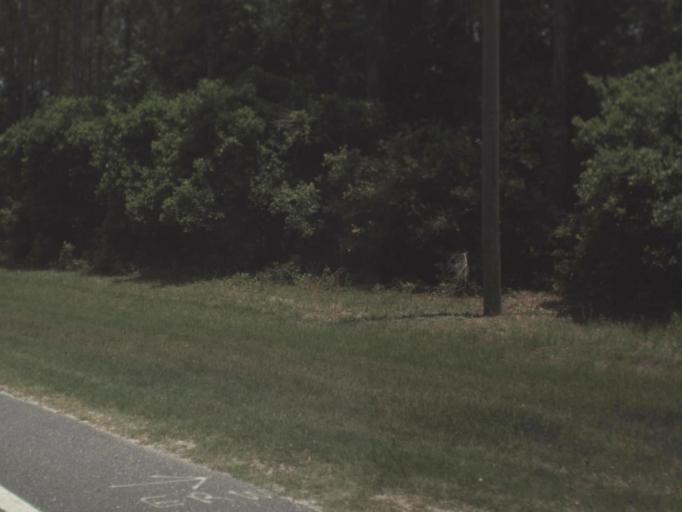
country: US
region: Florida
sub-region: Alachua County
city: Newberry
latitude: 29.6464
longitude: -82.6376
